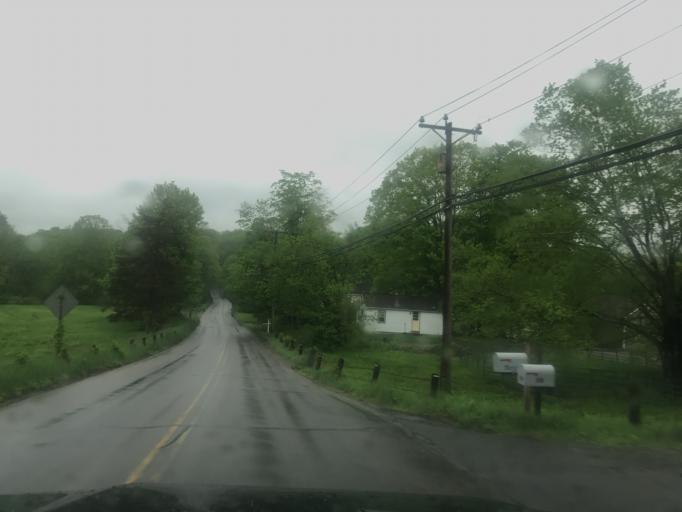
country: US
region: Connecticut
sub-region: Fairfield County
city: Bethel
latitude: 41.3097
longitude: -73.3629
